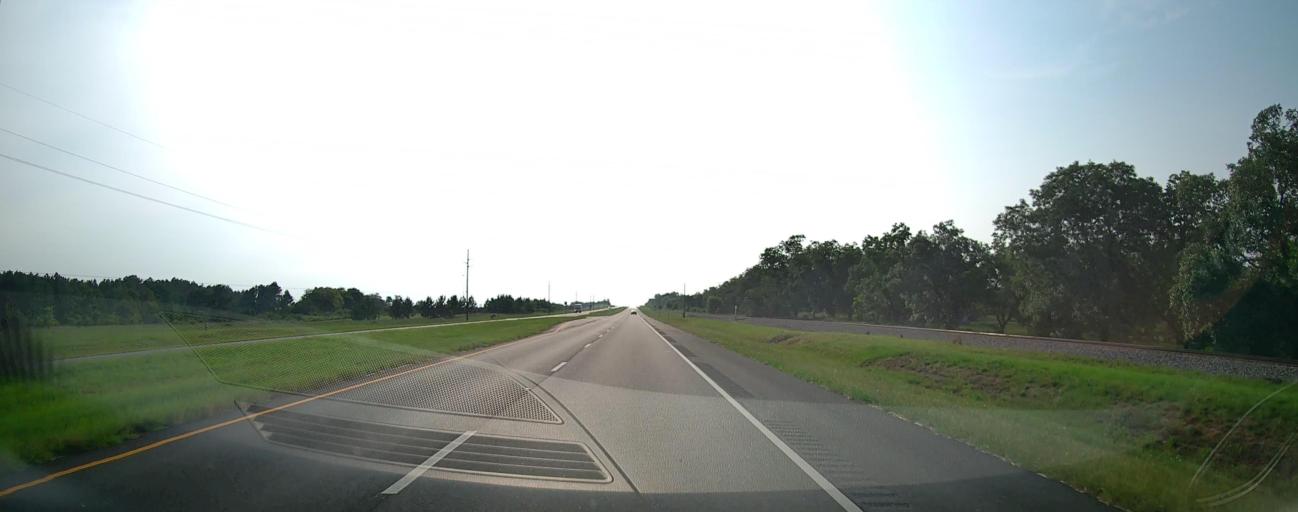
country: US
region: Georgia
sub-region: Taylor County
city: Butler
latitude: 32.5759
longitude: -84.3046
